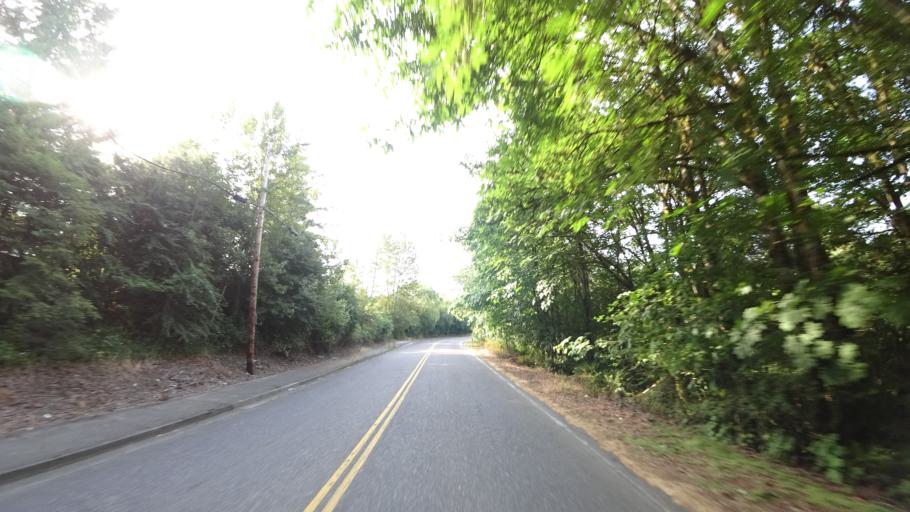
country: US
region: Oregon
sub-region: Clackamas County
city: Happy Valley
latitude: 45.4628
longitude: -122.5283
